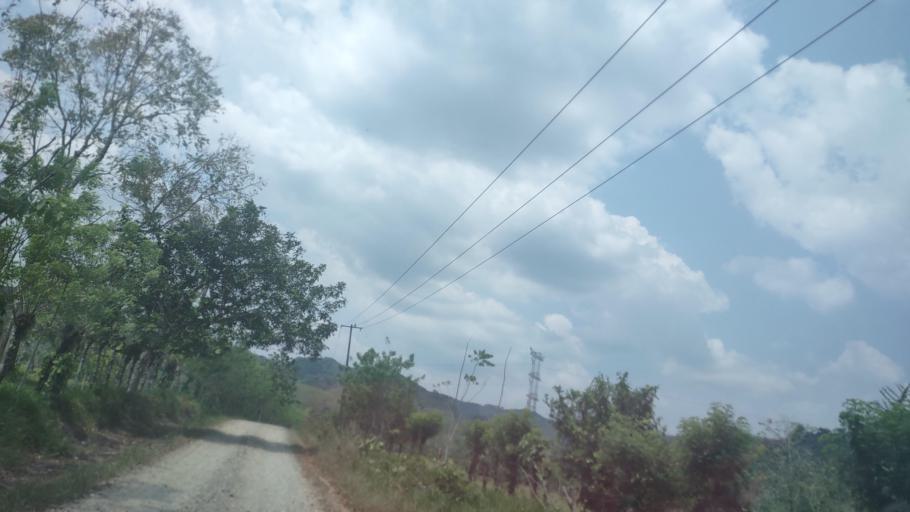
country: MX
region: Chiapas
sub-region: Tecpatan
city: Raudales Malpaso
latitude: 17.2769
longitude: -93.8705
